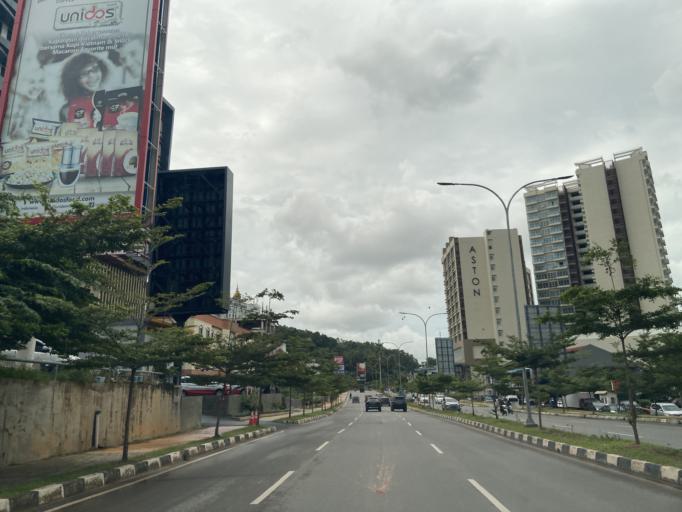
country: SG
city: Singapore
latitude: 1.1443
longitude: 104.0192
